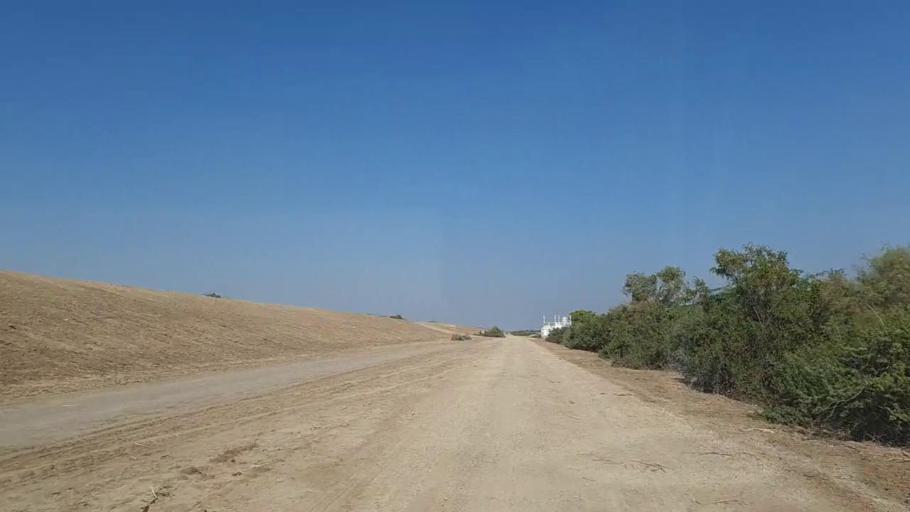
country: PK
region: Sindh
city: Chuhar Jamali
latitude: 24.4638
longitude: 68.0039
